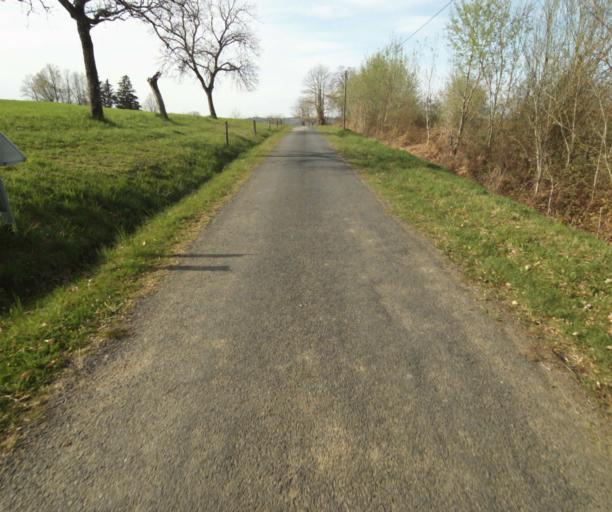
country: FR
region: Limousin
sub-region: Departement de la Correze
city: Naves
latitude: 45.3022
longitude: 1.7337
